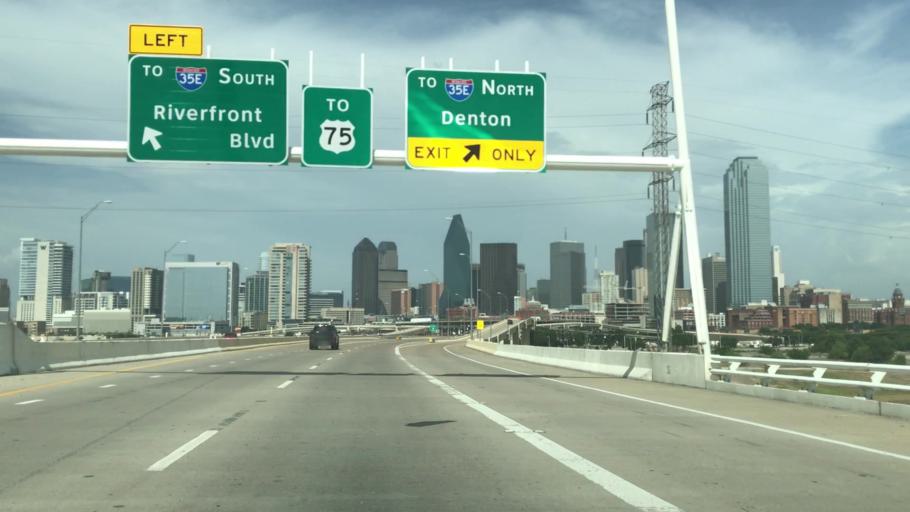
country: US
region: Texas
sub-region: Dallas County
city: Dallas
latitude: 32.7807
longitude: -96.8198
